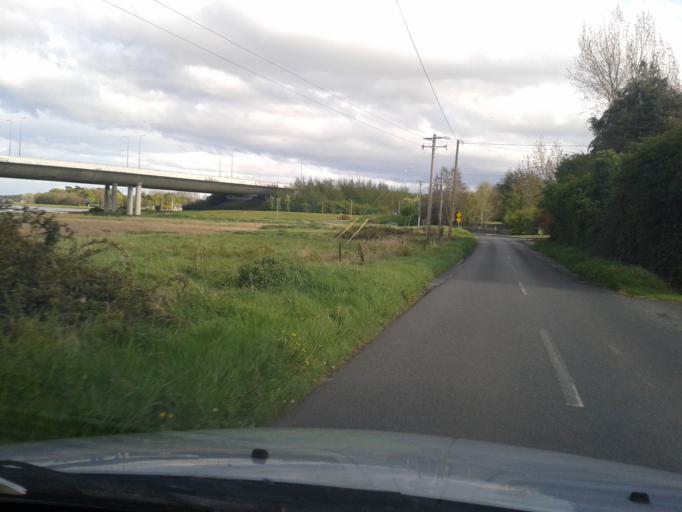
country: IE
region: Leinster
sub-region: Fingal County
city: Swords
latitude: 53.4661
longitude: -6.2061
